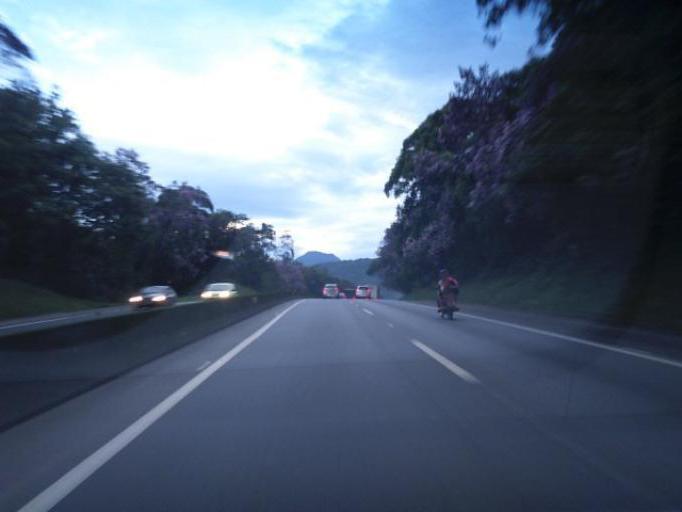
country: BR
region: Santa Catarina
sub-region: Joinville
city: Joinville
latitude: -26.1342
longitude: -48.8969
